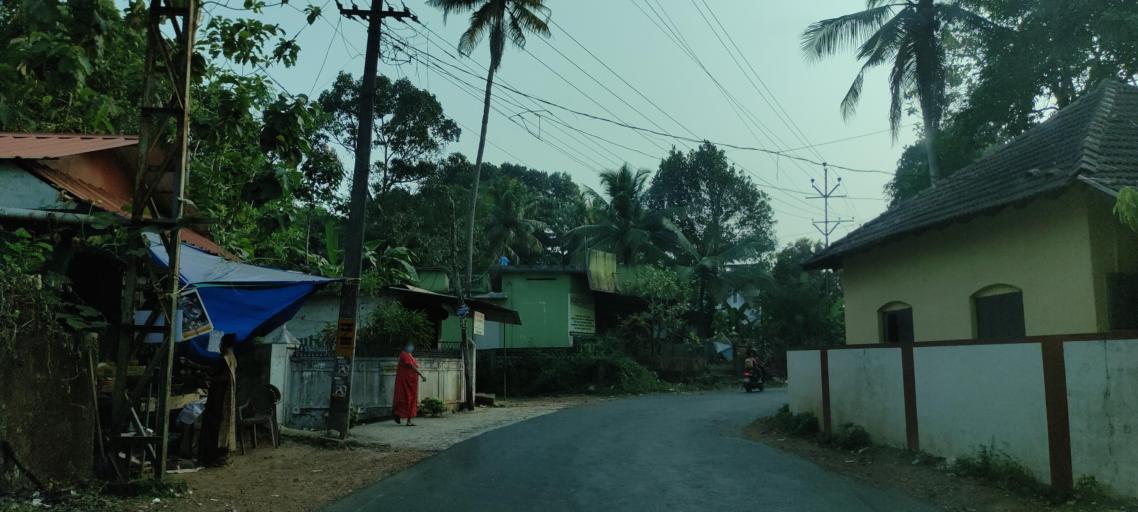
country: IN
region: Kerala
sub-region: Kottayam
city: Vaikam
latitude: 9.7226
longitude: 76.4774
